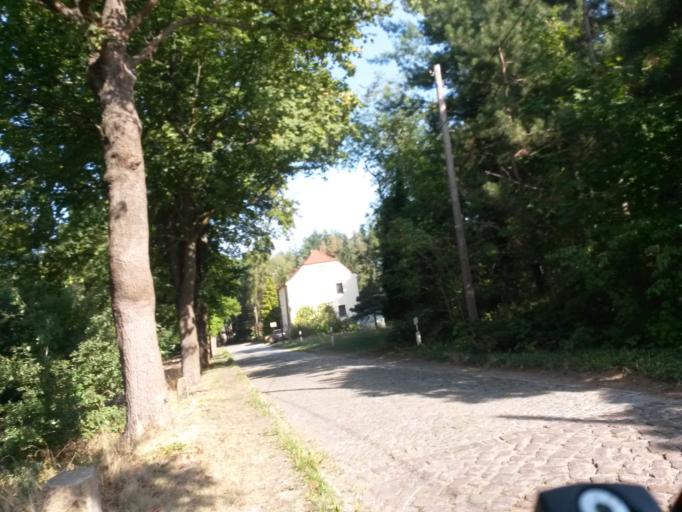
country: DE
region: Saxony-Anhalt
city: Nudersdorf
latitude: 51.9154
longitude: 12.5940
